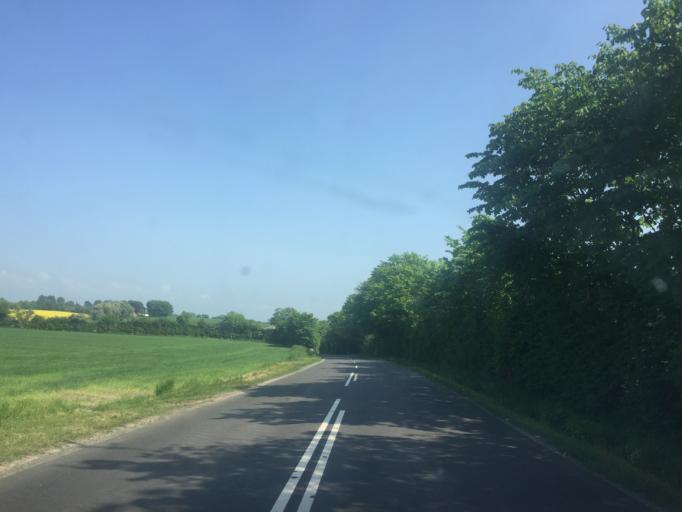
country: DK
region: South Denmark
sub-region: Kolding Kommune
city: Kolding
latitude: 55.4730
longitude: 9.5204
